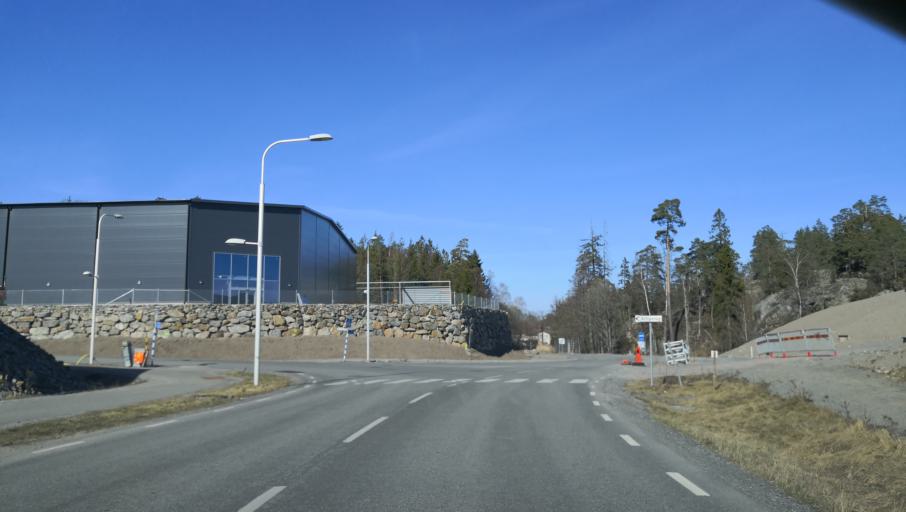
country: SE
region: Stockholm
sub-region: Varmdo Kommun
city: Gustavsberg
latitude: 59.3130
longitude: 18.3700
